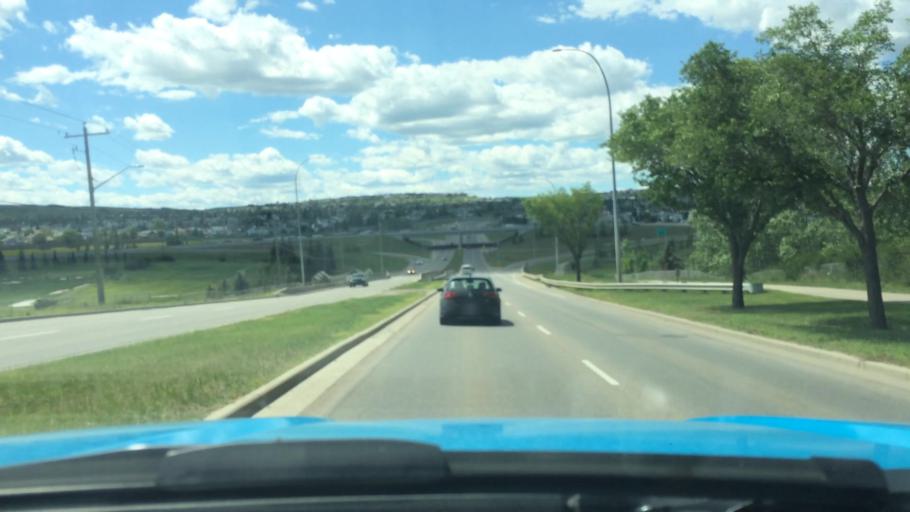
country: CA
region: Alberta
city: Calgary
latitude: 51.1456
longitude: -114.0864
